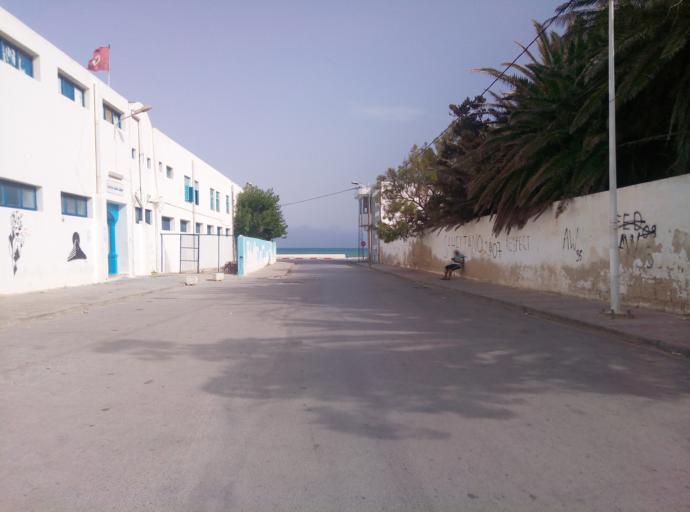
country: TN
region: Nabul
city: Al Hammamat
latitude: 36.3942
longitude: 10.6177
